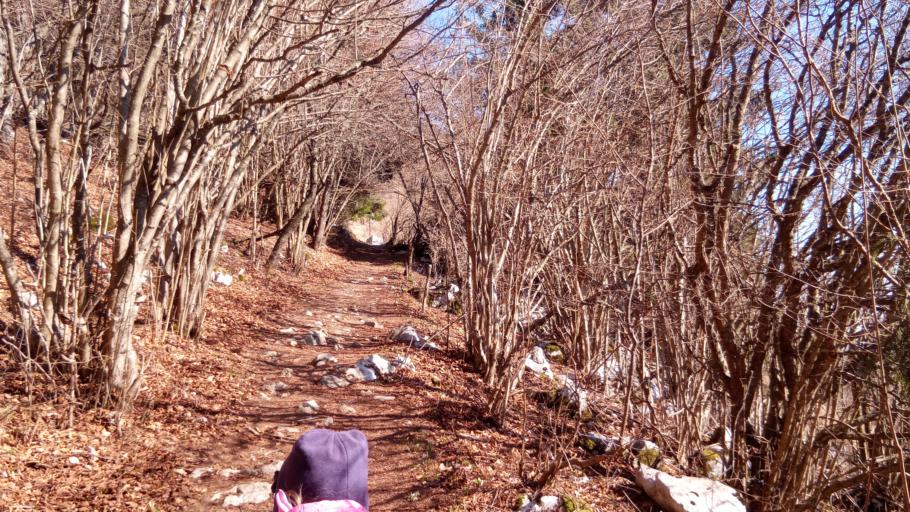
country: IT
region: Veneto
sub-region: Provincia di Treviso
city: Borso del Grappa
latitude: 45.8412
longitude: 11.7847
